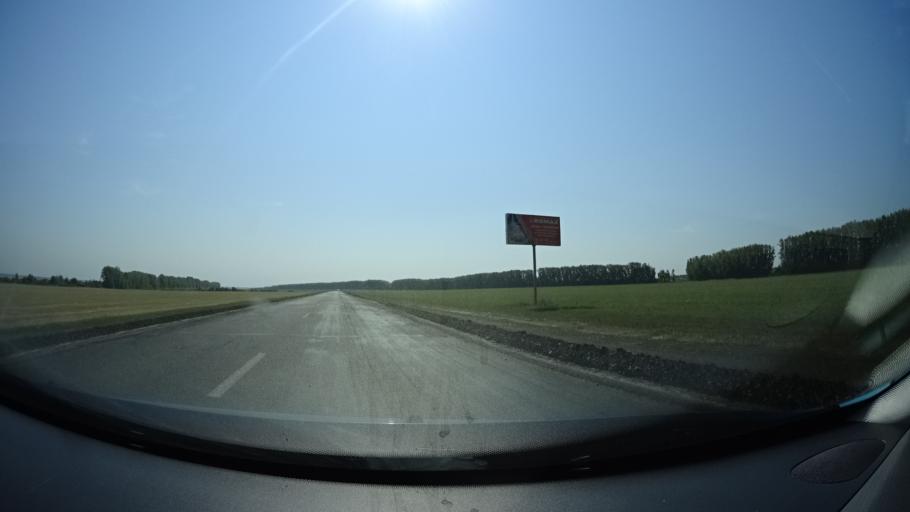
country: RU
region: Bashkortostan
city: Kabakovo
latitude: 54.4610
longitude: 55.9644
